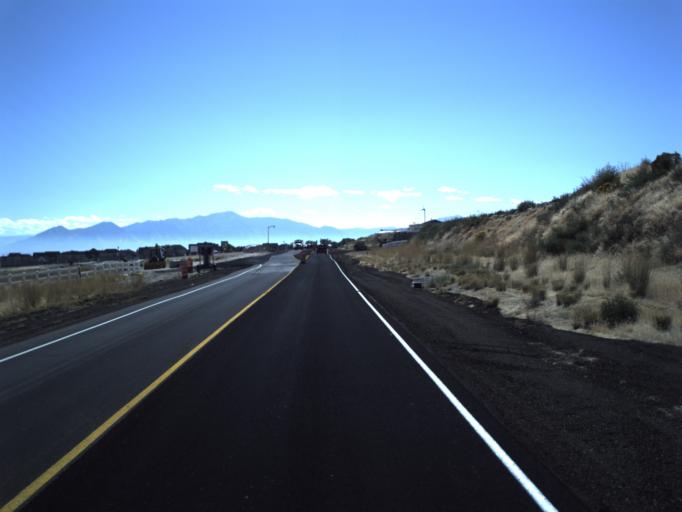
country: US
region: Utah
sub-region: Utah County
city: Saratoga Springs
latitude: 40.2973
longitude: -111.8829
